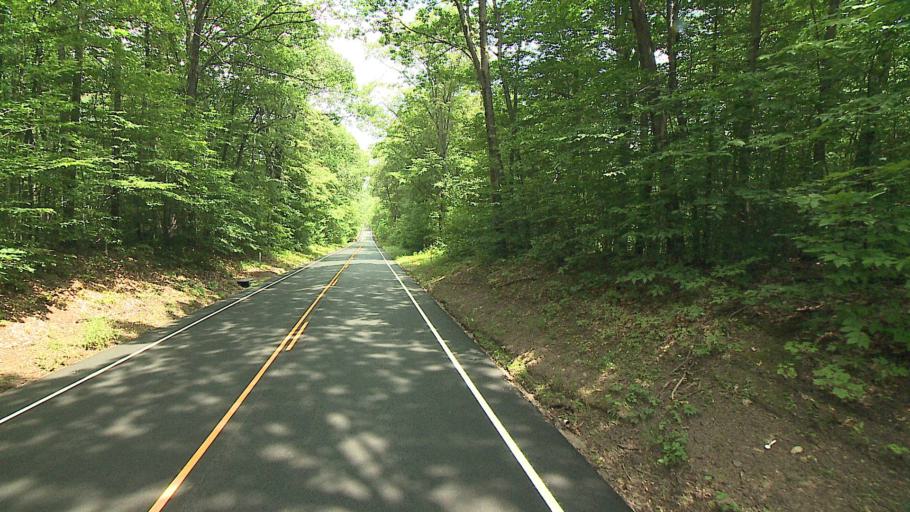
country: US
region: Massachusetts
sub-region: Hampden County
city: Granville
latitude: 42.0155
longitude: -72.8914
